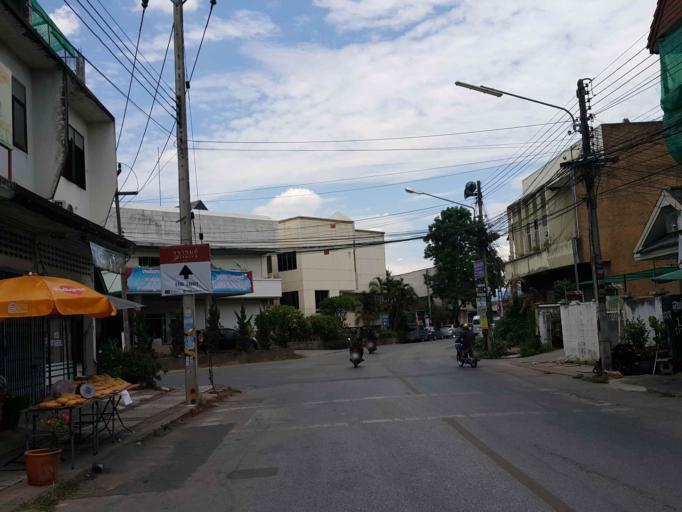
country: TH
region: Chiang Mai
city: Chiang Mai
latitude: 18.7842
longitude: 99.0121
